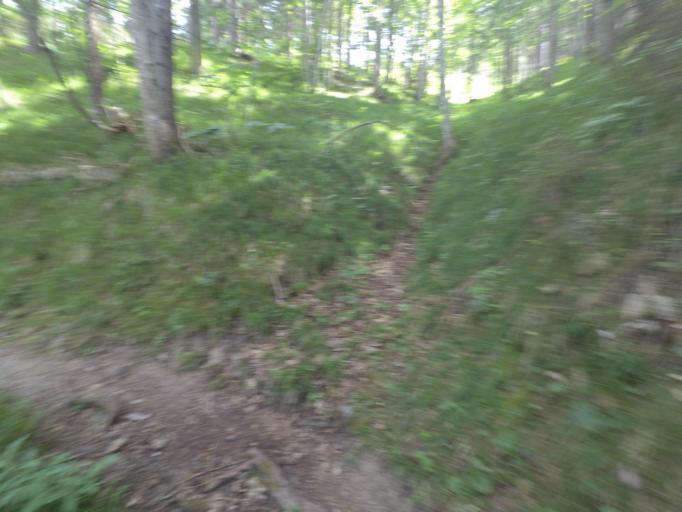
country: AT
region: Salzburg
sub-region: Politischer Bezirk Zell am See
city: Saalfelden am Steinernen Meer
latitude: 47.4456
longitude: 12.8569
